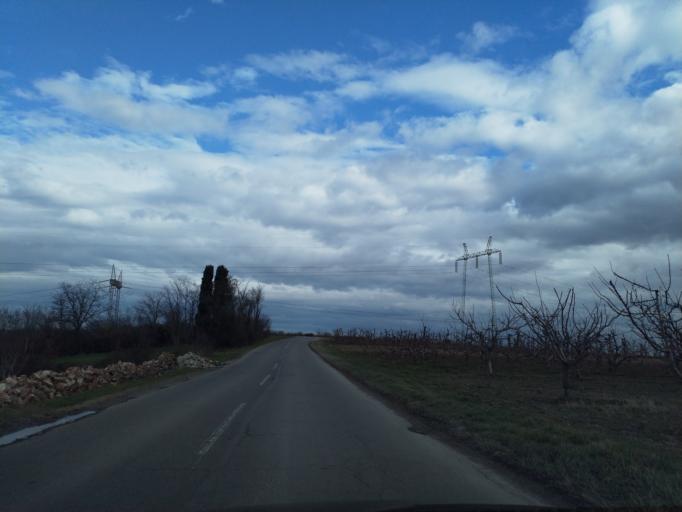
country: RS
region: Central Serbia
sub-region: Belgrade
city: Grocka
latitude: 44.6300
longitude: 20.7464
